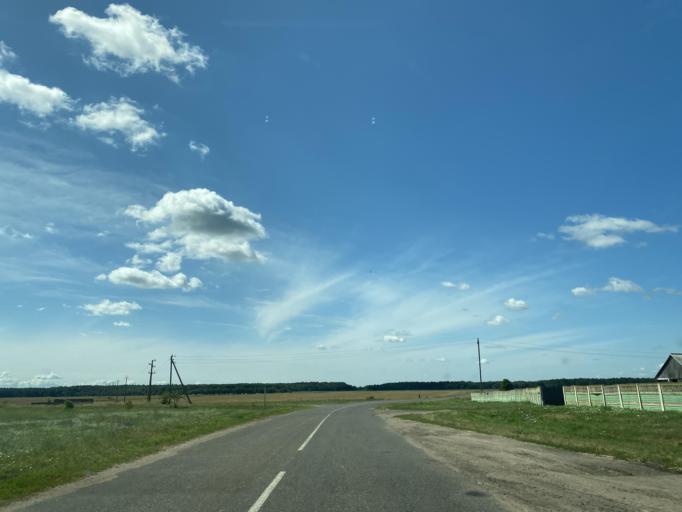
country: BY
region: Brest
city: Ivanava
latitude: 52.2334
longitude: 25.6518
